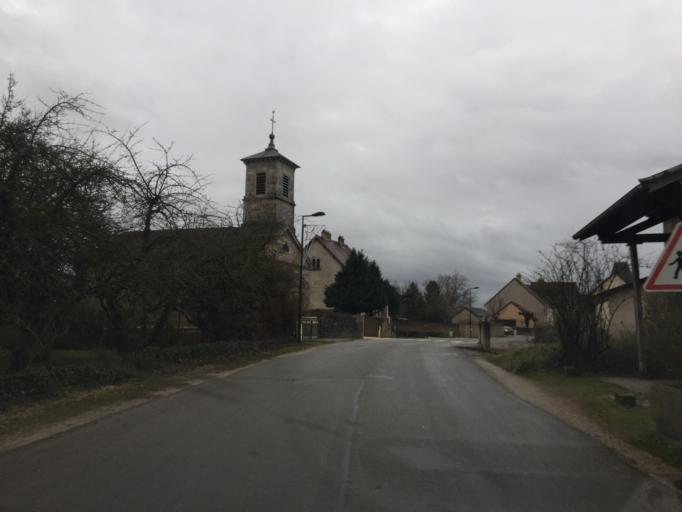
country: FR
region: Franche-Comte
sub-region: Departement du Jura
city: Dole
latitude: 47.1468
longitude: 5.5525
